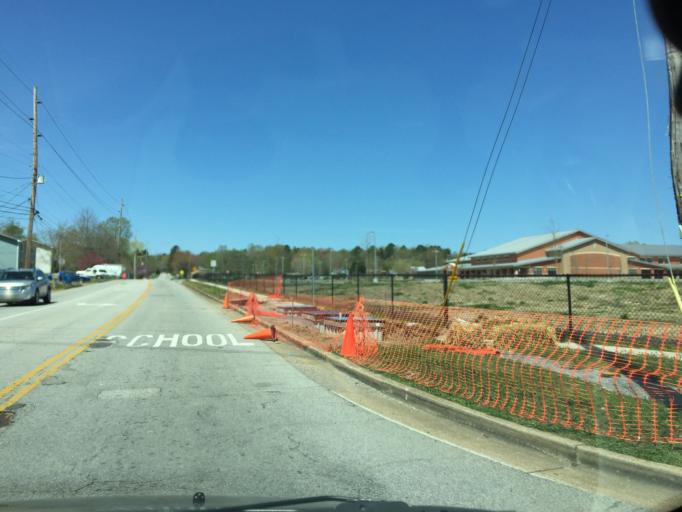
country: US
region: Tennessee
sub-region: Hamilton County
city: Middle Valley
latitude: 35.1892
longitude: -85.1900
